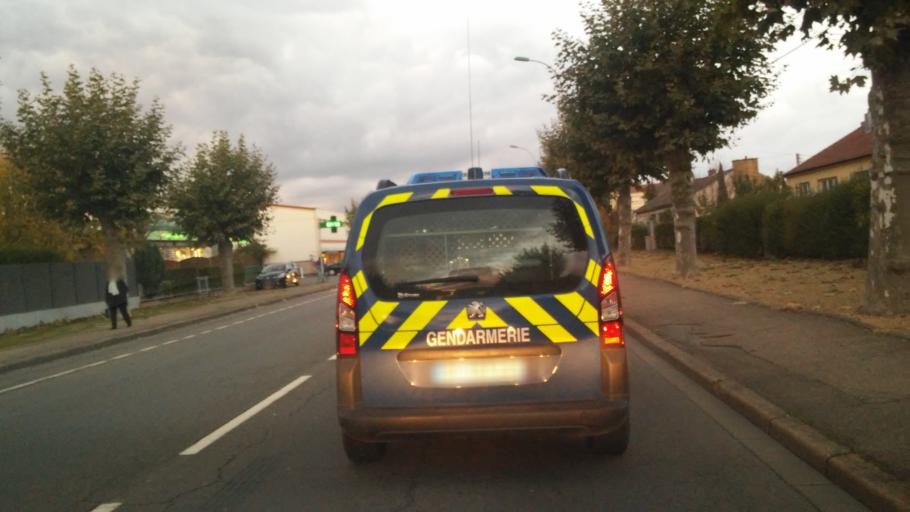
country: FR
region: Lorraine
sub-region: Departement de la Moselle
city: Maizieres-les-Metz
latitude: 49.2035
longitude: 6.1608
